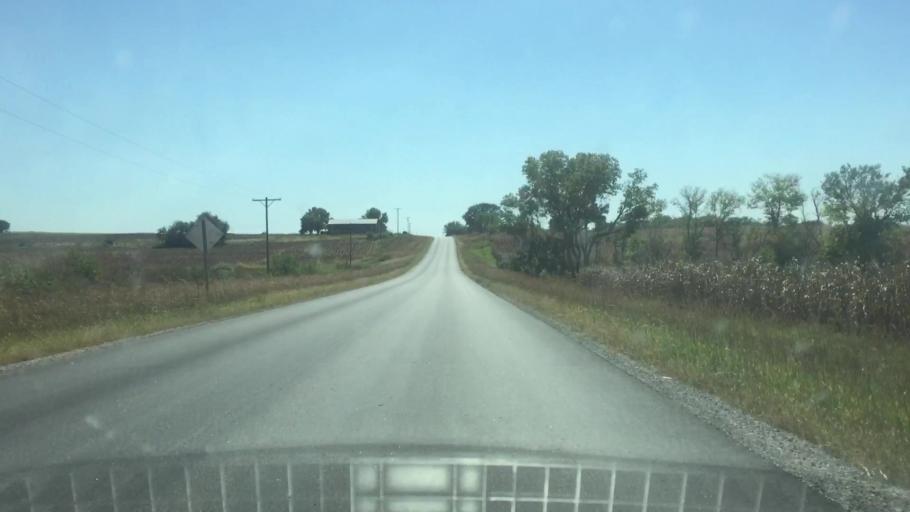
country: US
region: Kansas
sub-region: Marshall County
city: Marysville
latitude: 39.9568
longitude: -96.6009
